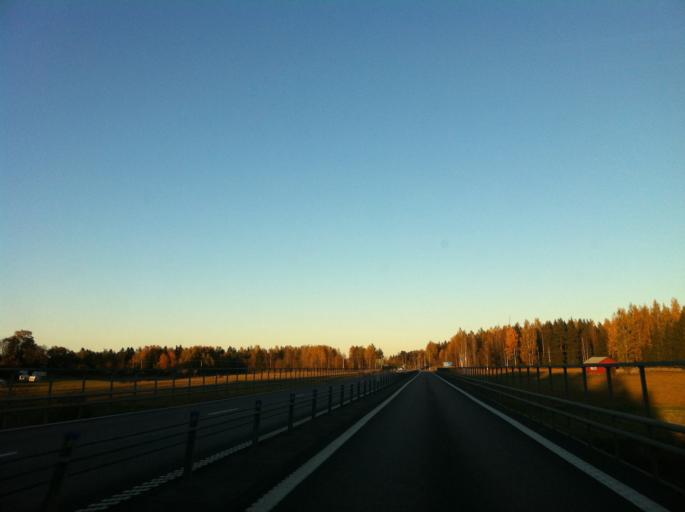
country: SE
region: Gaevleborg
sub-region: Sandvikens Kommun
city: Jarbo
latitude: 60.5978
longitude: 16.5786
